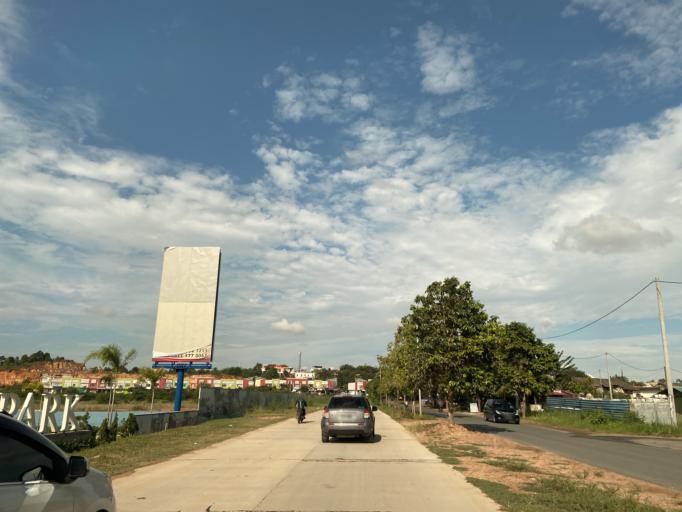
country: SG
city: Singapore
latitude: 1.1118
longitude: 104.0742
